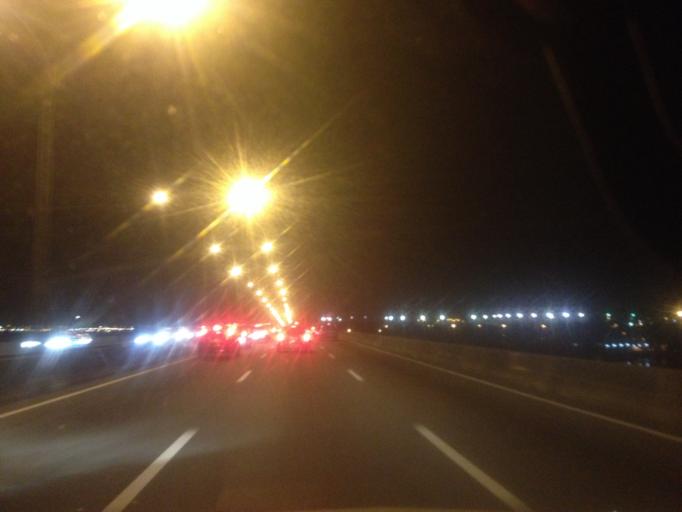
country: BR
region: Rio de Janeiro
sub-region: Rio De Janeiro
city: Rio de Janeiro
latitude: -22.8359
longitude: -43.2445
